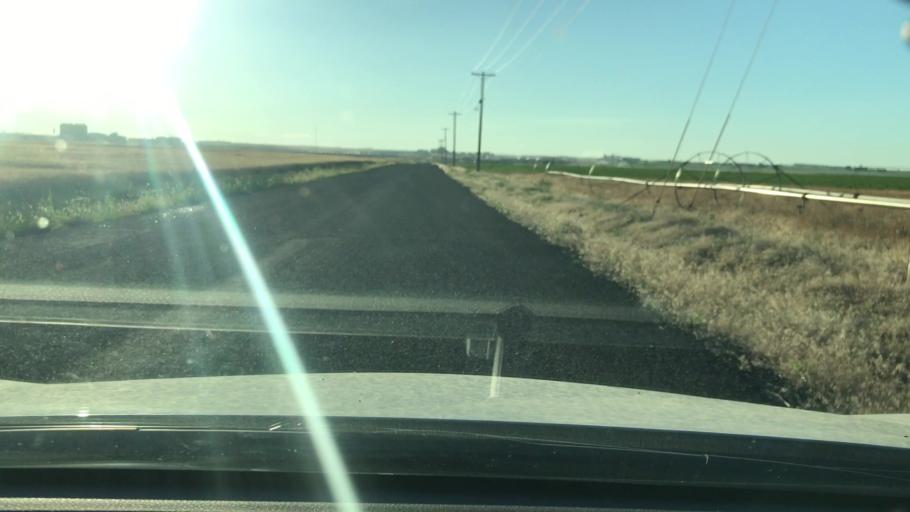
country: US
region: Washington
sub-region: Grant County
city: Moses Lake
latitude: 47.1163
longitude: -119.2351
